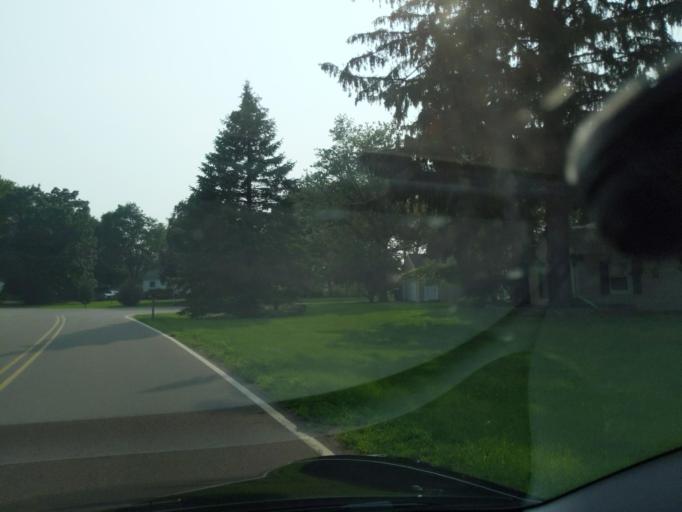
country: US
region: Michigan
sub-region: Jackson County
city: Jackson
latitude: 42.2397
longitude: -84.4446
